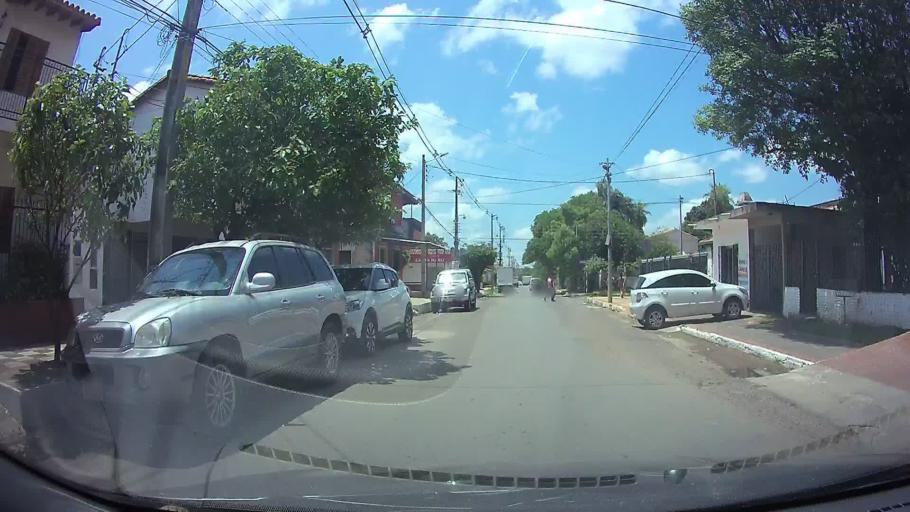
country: PY
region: Central
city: Fernando de la Mora
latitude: -25.2983
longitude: -57.5481
